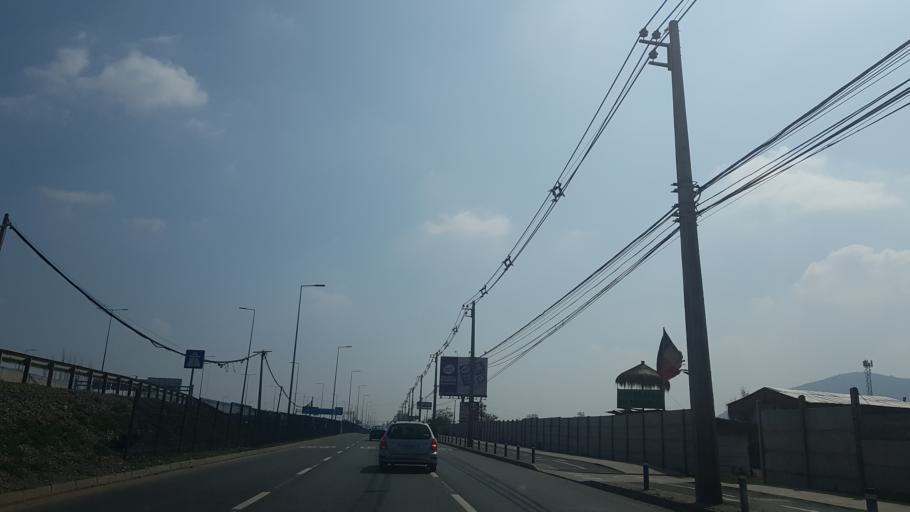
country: CL
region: Santiago Metropolitan
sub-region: Provincia de Chacabuco
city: Chicureo Abajo
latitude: -33.3542
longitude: -70.7052
